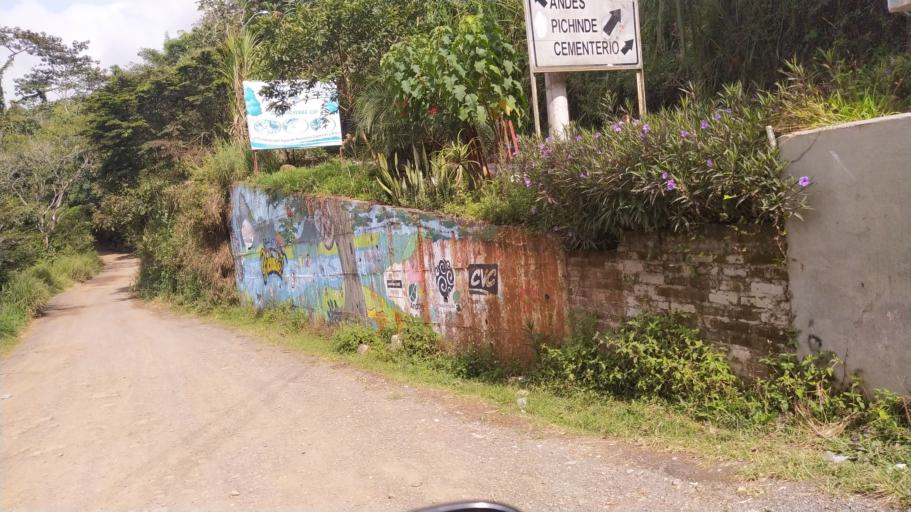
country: CO
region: Valle del Cauca
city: Cali
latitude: 3.4347
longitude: -76.6132
